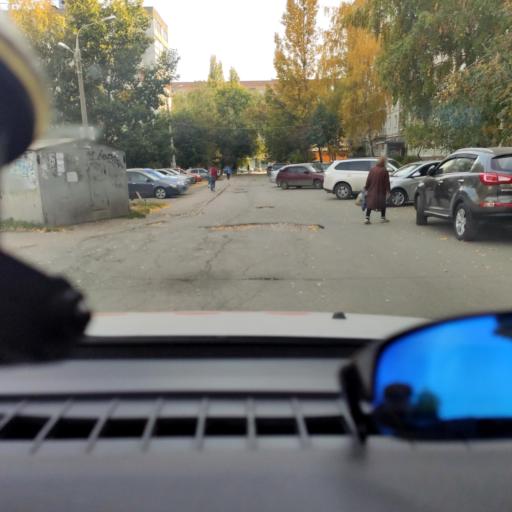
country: RU
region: Samara
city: Samara
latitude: 53.2376
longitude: 50.2223
